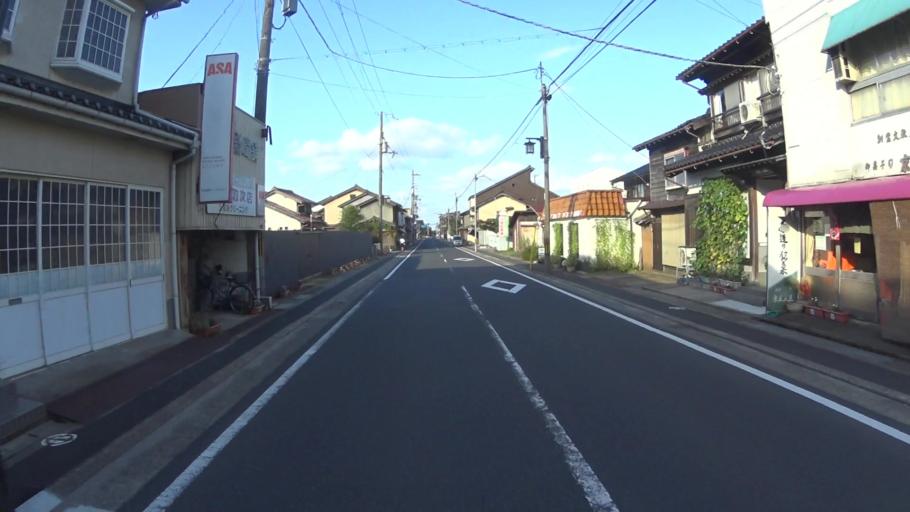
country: JP
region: Hyogo
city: Toyooka
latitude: 35.6040
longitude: 134.8950
